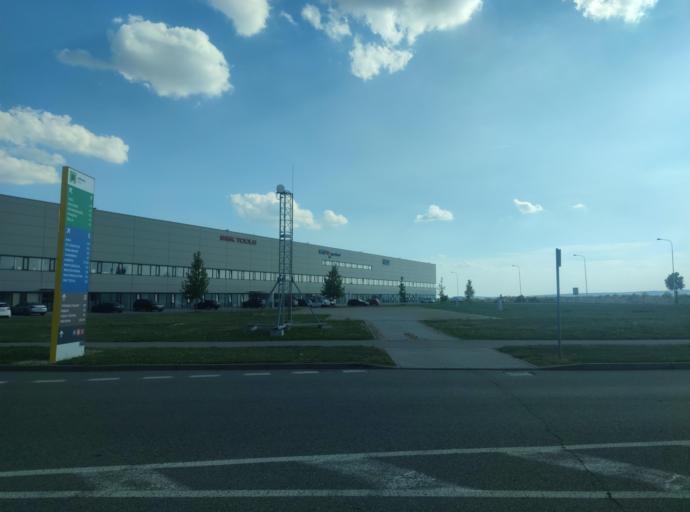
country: CZ
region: South Moravian
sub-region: Mesto Brno
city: Brno
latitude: 49.1822
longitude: 16.6567
